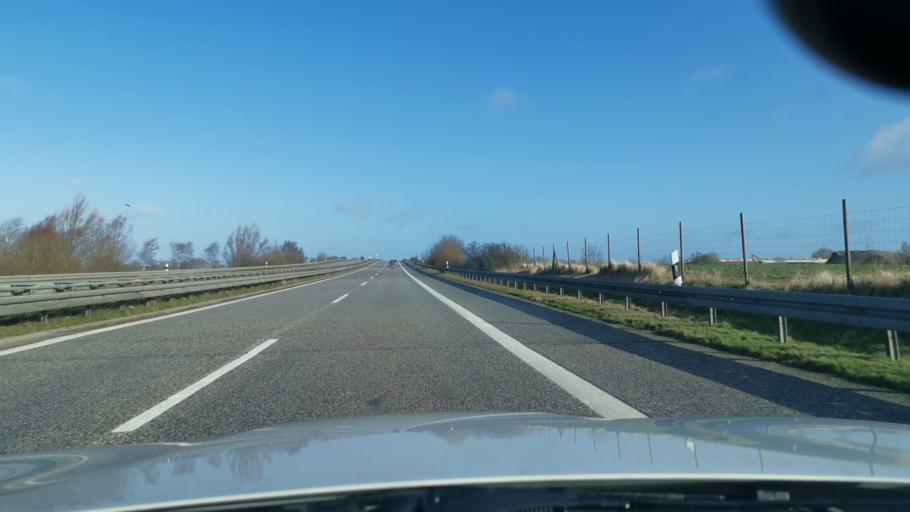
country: DE
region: Mecklenburg-Vorpommern
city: Kritzmow
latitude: 54.0710
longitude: 12.0512
